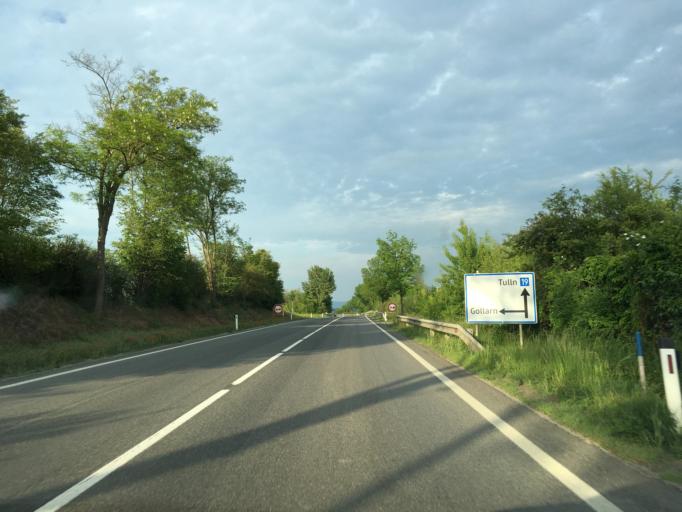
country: AT
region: Lower Austria
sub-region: Politischer Bezirk Tulln
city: Sieghartskirchen
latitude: 48.2739
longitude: 15.9838
